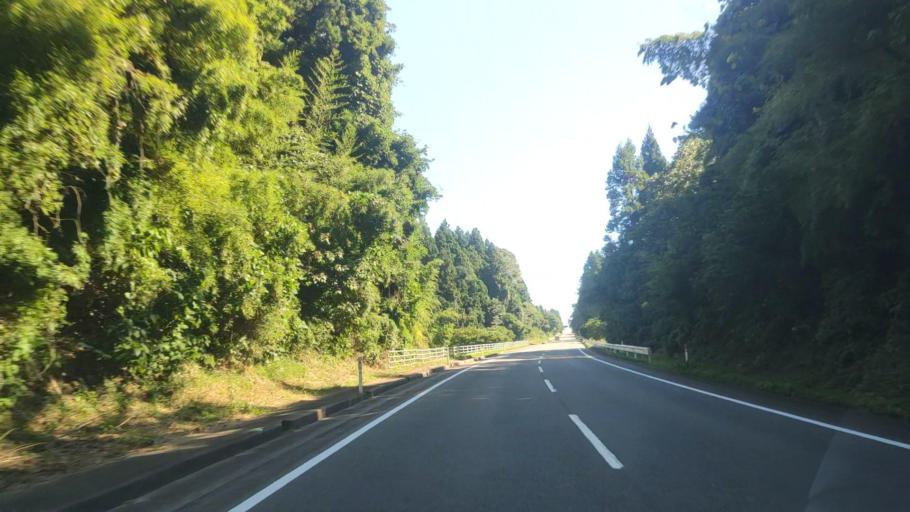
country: JP
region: Ishikawa
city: Nanao
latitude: 37.3754
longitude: 137.2343
